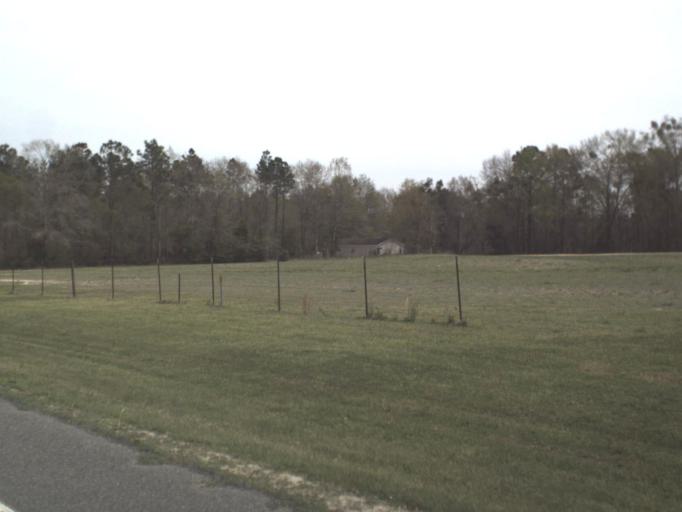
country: US
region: Alabama
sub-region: Geneva County
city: Geneva
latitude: 30.9531
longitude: -85.9180
